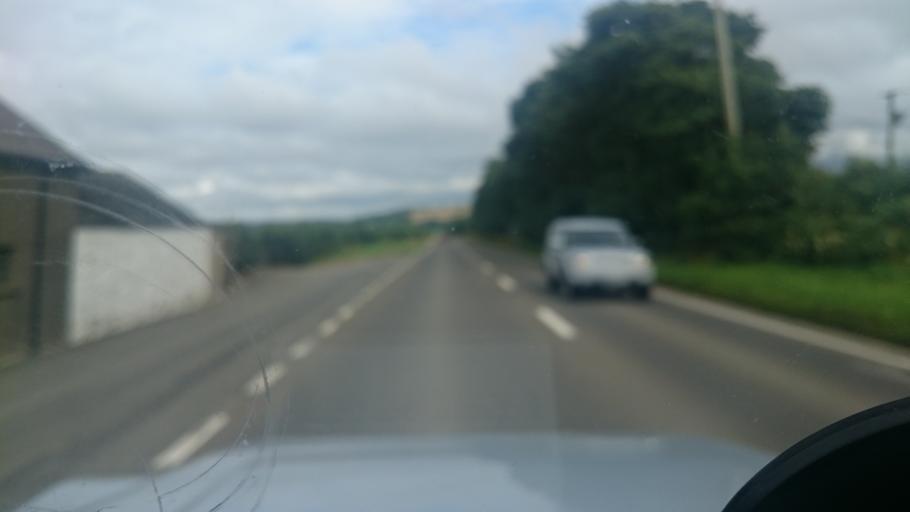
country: GB
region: Wales
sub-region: Pembrokeshire
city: Hook
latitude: 51.8053
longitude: -4.9171
